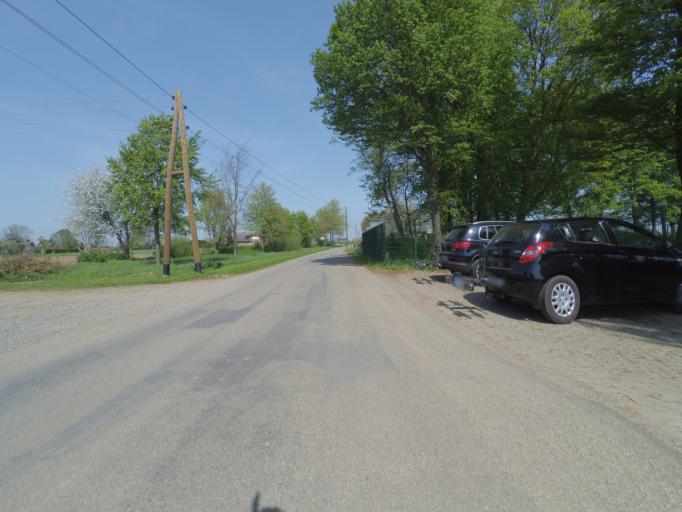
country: DE
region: North Rhine-Westphalia
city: Rees
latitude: 51.8140
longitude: 6.3942
